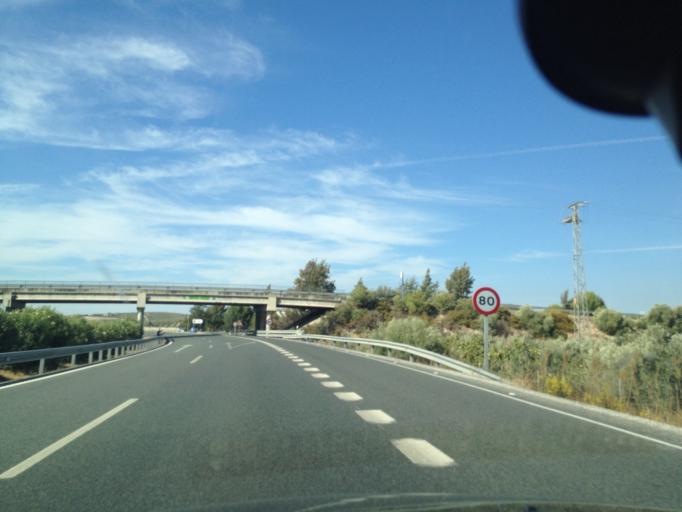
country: ES
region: Andalusia
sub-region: Provincia de Sevilla
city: Aguadulce
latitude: 37.2501
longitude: -5.0083
